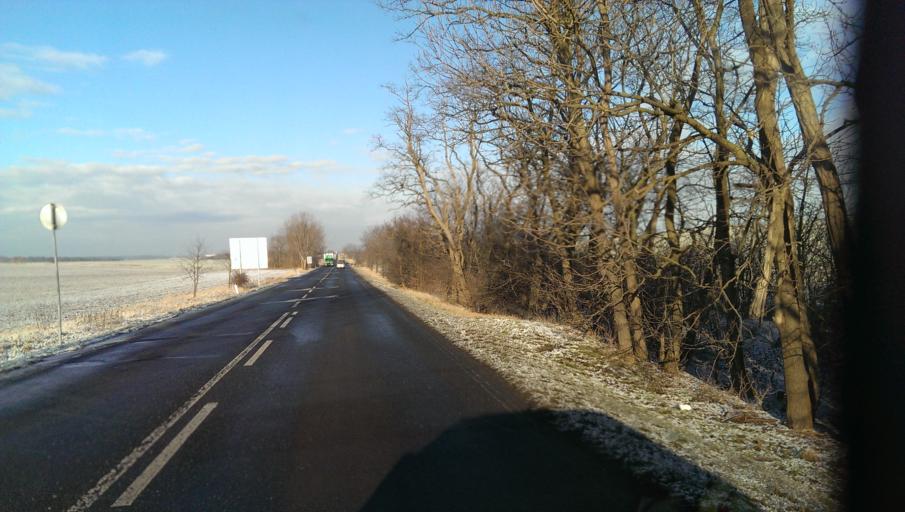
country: CZ
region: Ustecky
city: Roudnice nad Labem
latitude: 50.3918
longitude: 14.2237
